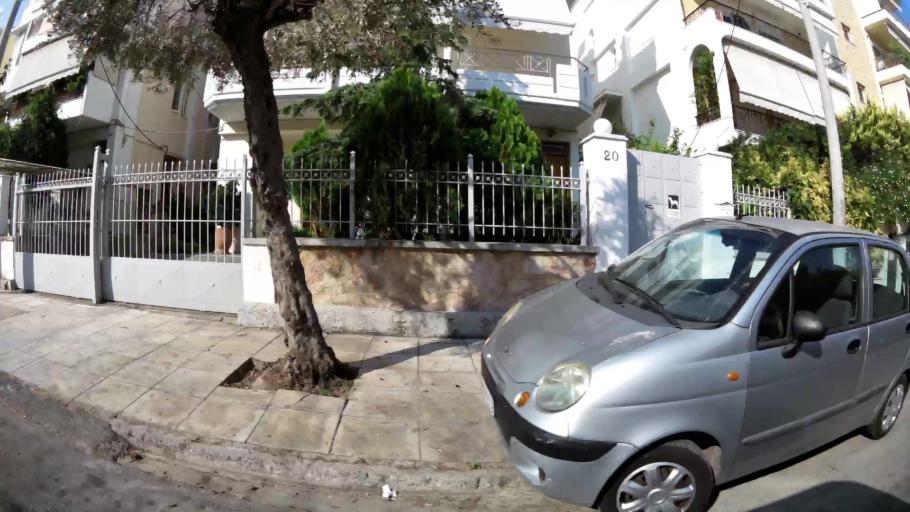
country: GR
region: Attica
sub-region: Nomarchia Athinas
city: Palaio Faliro
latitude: 37.9356
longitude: 23.7034
